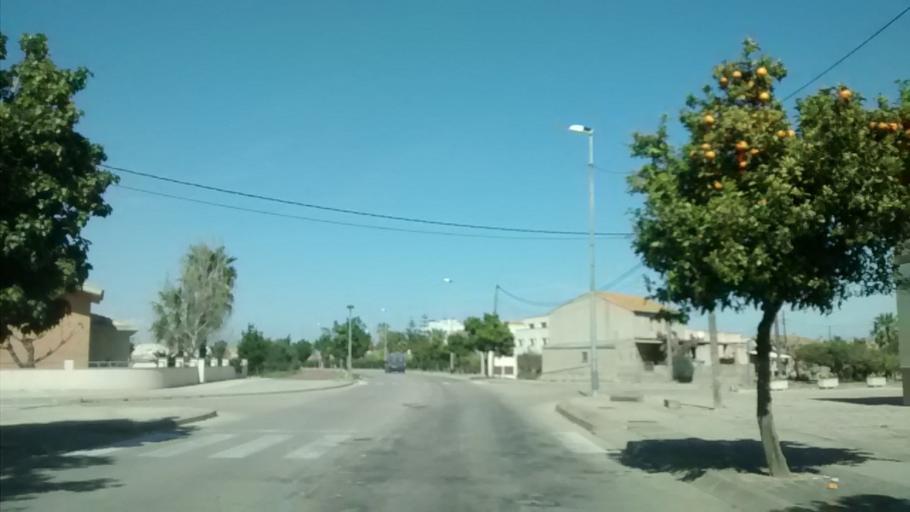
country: ES
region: Catalonia
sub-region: Provincia de Tarragona
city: Deltebre
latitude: 40.7164
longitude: 0.7197
